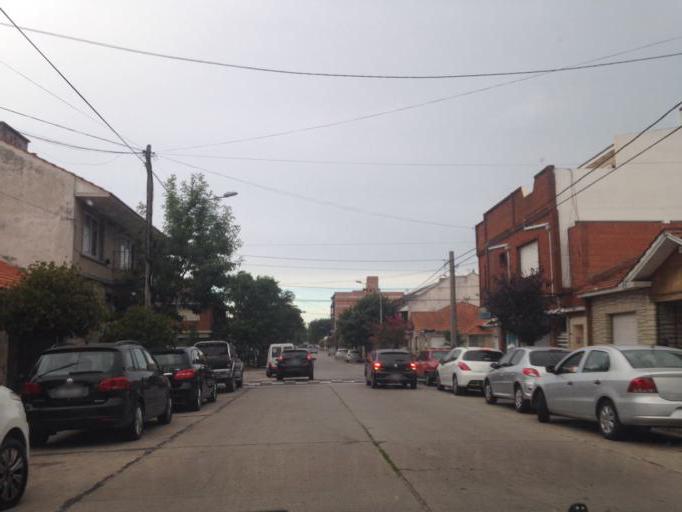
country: AR
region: Buenos Aires
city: Mar del Plata
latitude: -38.0180
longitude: -57.5682
